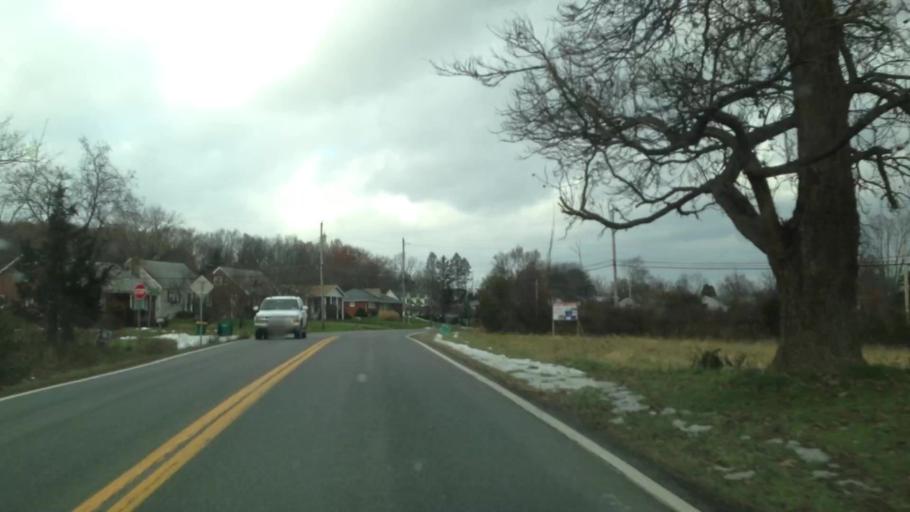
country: US
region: New York
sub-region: Ulster County
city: Glasco
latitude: 42.0310
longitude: -73.9565
